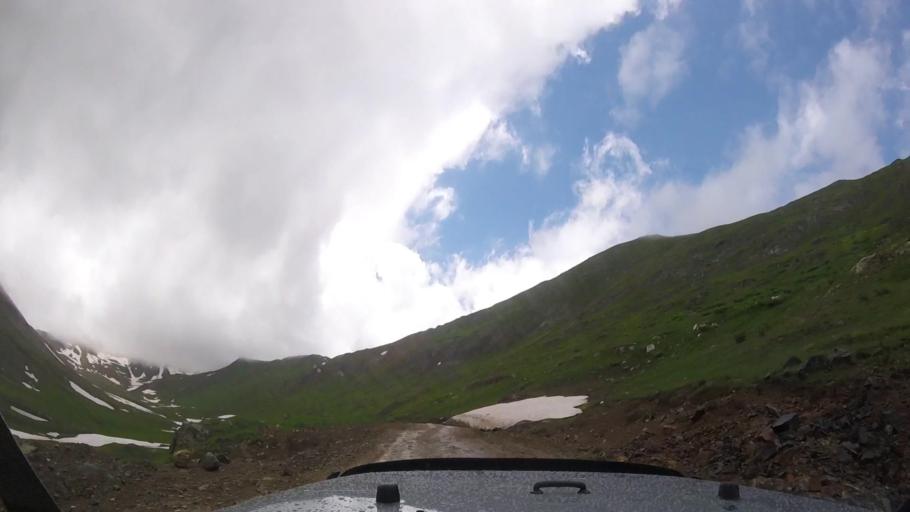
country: US
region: Colorado
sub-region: Ouray County
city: Ouray
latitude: 37.9304
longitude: -107.6046
